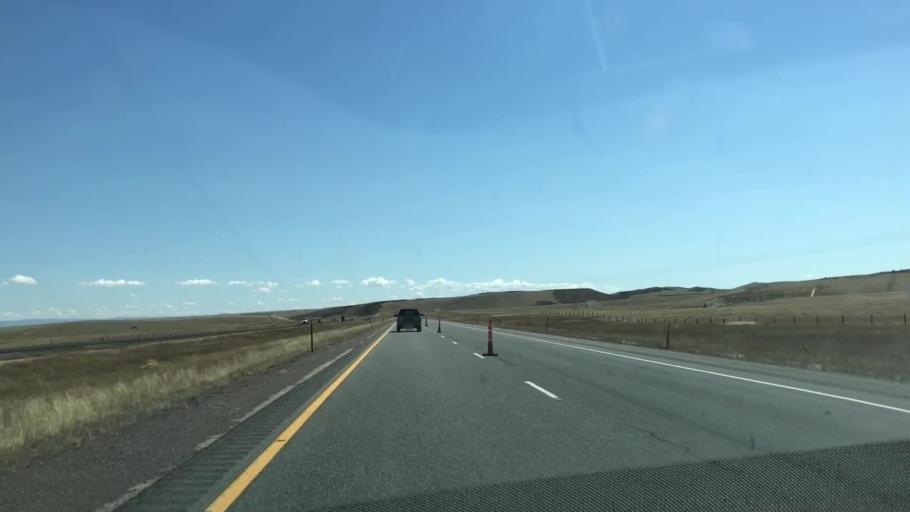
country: US
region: Wyoming
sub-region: Albany County
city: Laramie
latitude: 41.5710
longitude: -106.1507
